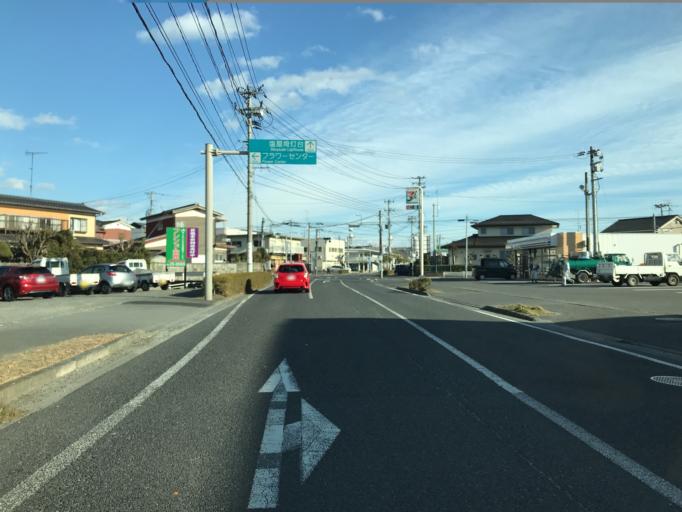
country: JP
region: Fukushima
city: Iwaki
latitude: 37.0637
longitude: 140.8944
